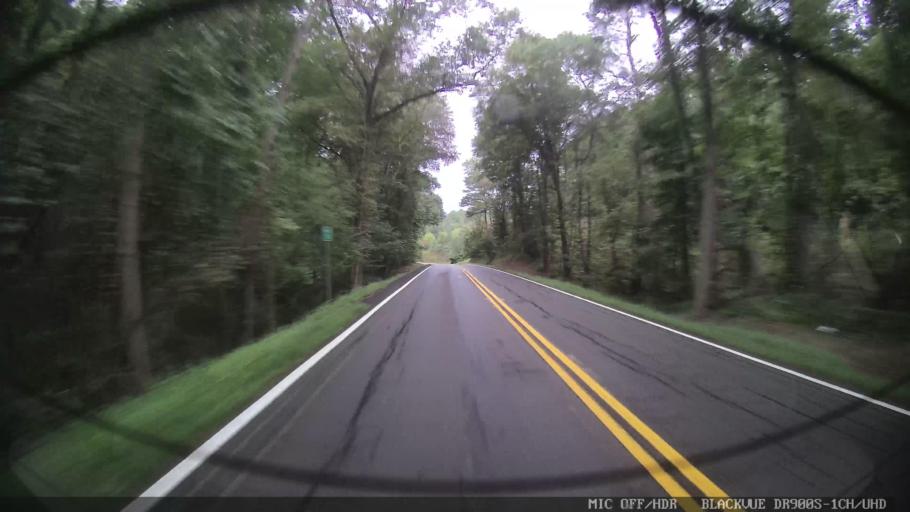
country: US
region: Georgia
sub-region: Gilmer County
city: Ellijay
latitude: 34.7390
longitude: -84.5198
